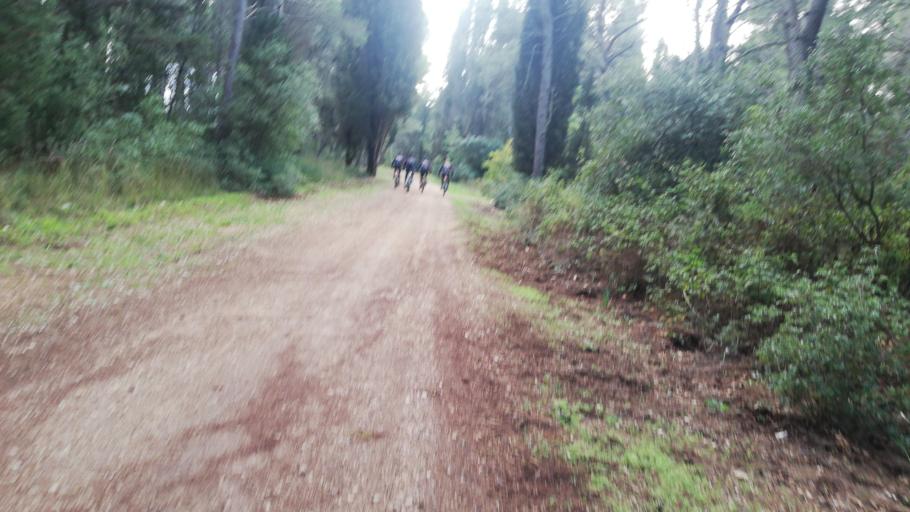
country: IT
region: Apulia
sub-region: Provincia di Bari
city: Cassano delle Murge
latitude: 40.8744
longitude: 16.7141
